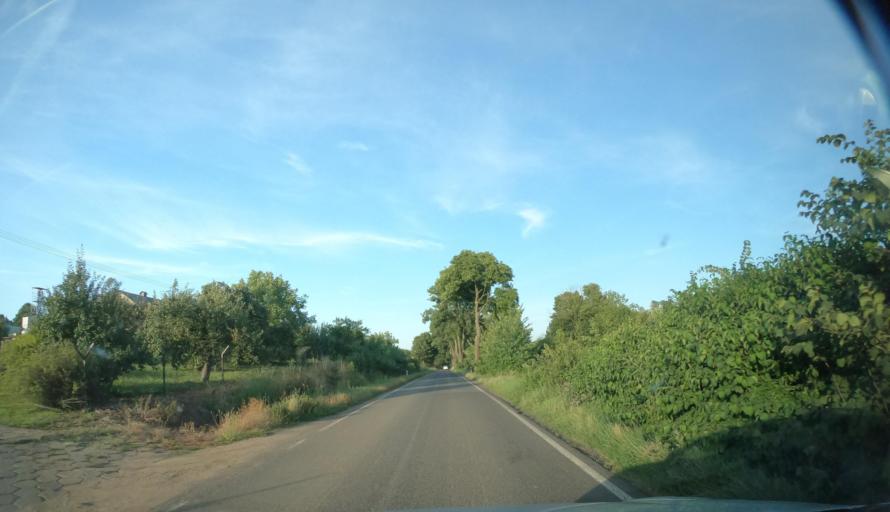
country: PL
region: Kujawsko-Pomorskie
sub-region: Bydgoszcz
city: Fordon
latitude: 53.2291
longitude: 18.2041
